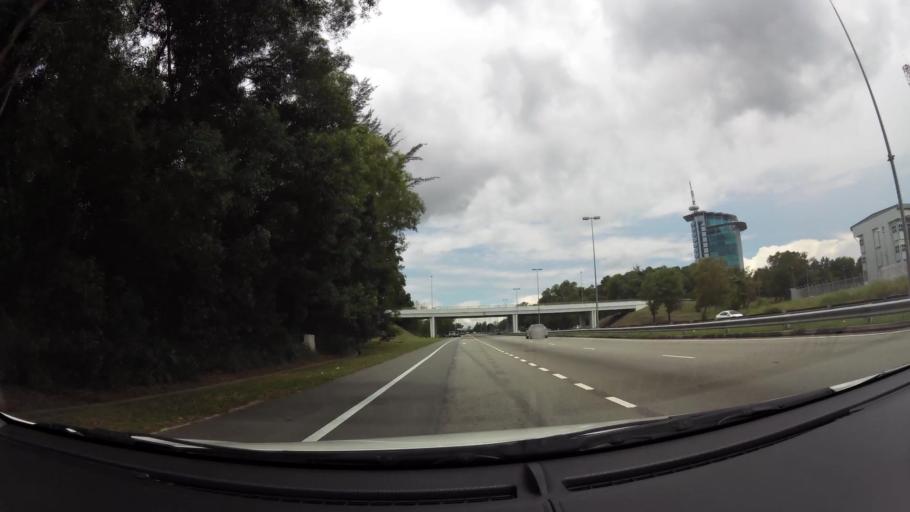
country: BN
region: Brunei and Muara
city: Bandar Seri Begawan
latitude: 4.9692
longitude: 114.8847
